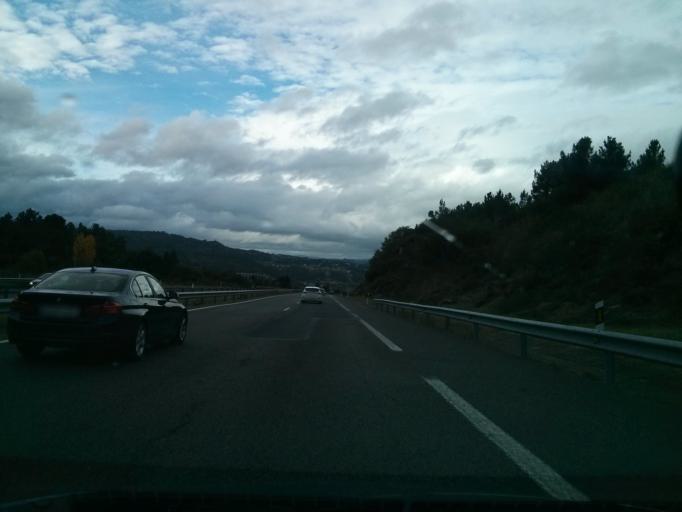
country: ES
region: Galicia
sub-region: Provincia de Ourense
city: Ourense
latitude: 42.2881
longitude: -7.8754
